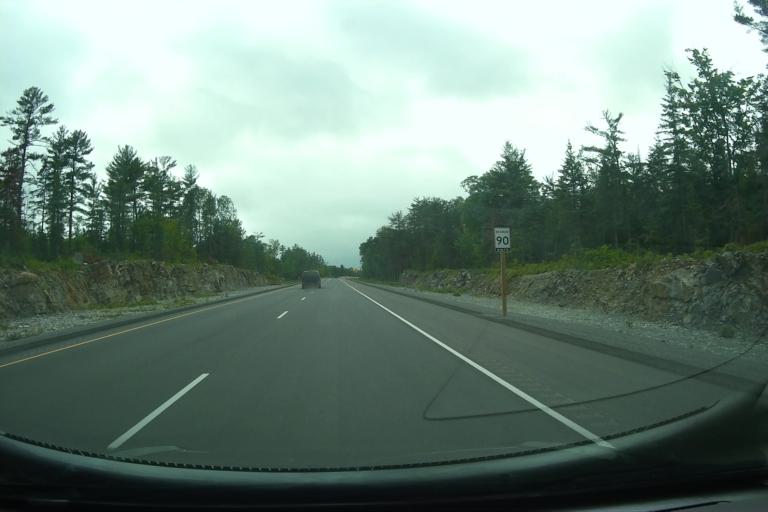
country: CA
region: Ontario
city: Arnprior
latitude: 45.4376
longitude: -76.4468
